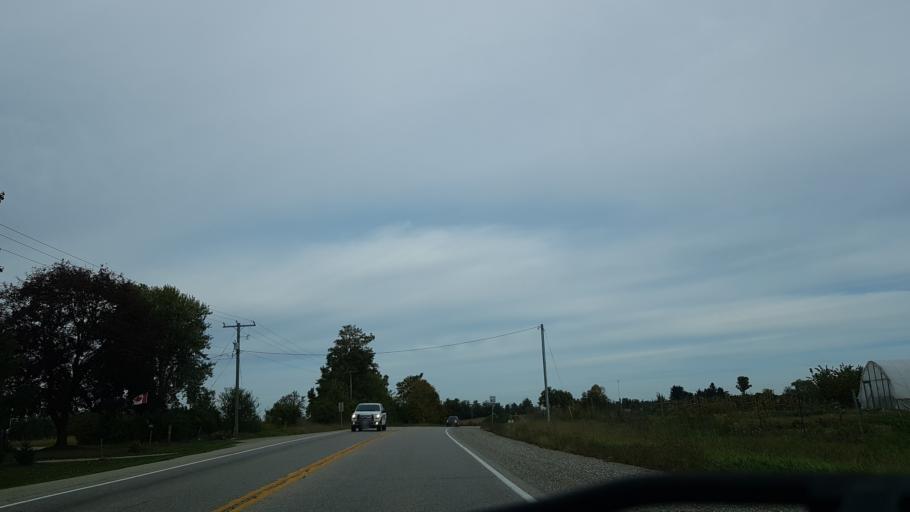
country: CA
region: Ontario
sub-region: Wellington County
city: Guelph
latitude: 43.6241
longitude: -80.2135
